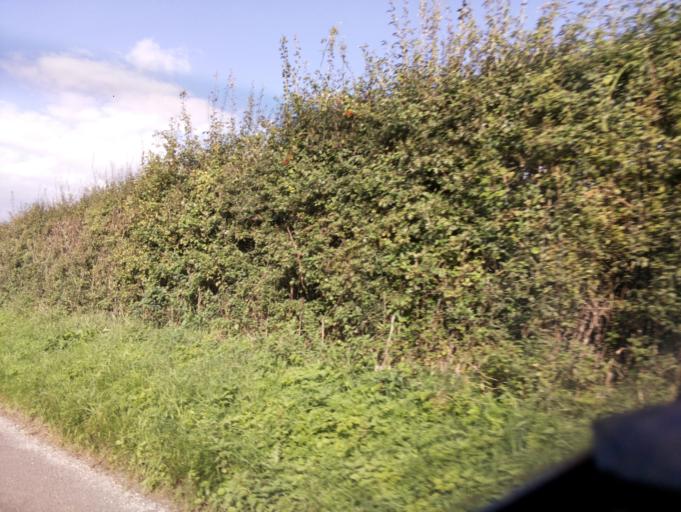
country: GB
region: England
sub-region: Hampshire
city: Chandlers Ford
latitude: 51.0554
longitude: -1.3824
